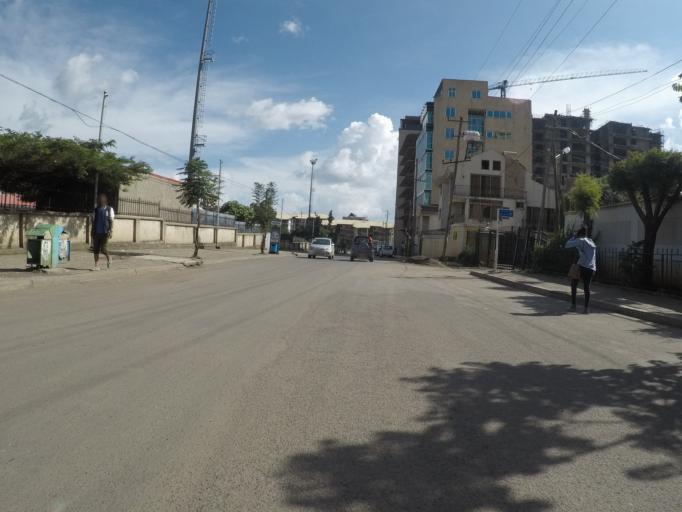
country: ET
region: Adis Abeba
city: Addis Ababa
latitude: 8.9912
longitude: 38.7882
